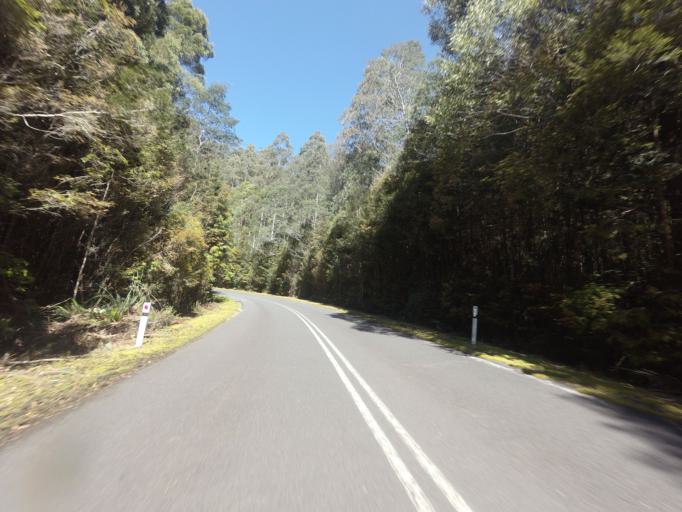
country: AU
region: Tasmania
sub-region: Huon Valley
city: Geeveston
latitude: -42.8276
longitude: 146.3174
